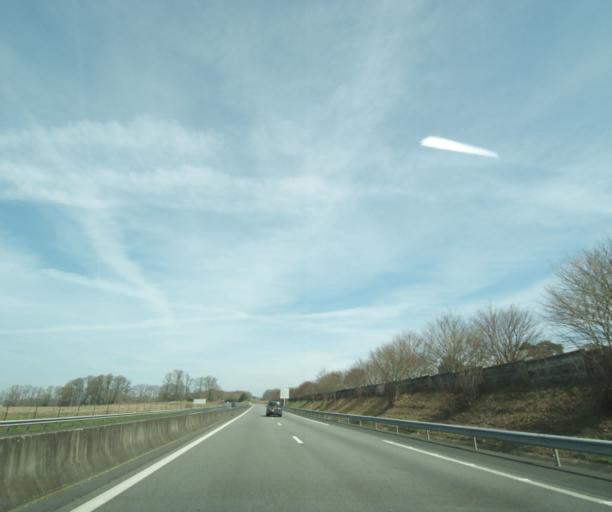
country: FR
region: Limousin
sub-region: Departement de la Correze
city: Uzerche
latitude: 45.3813
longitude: 1.5747
